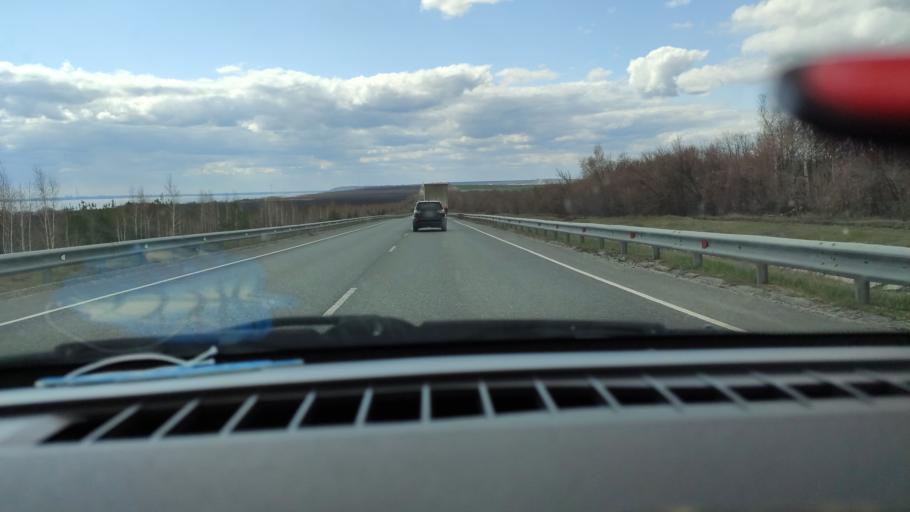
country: RU
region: Saratov
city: Balakovo
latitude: 52.1528
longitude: 47.8131
